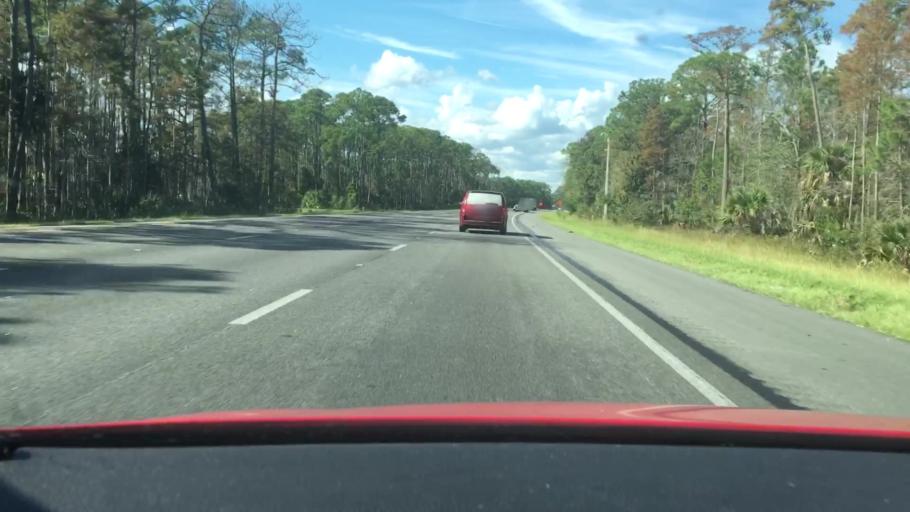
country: US
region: Florida
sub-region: Volusia County
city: Port Orange
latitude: 29.1301
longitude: -81.0595
